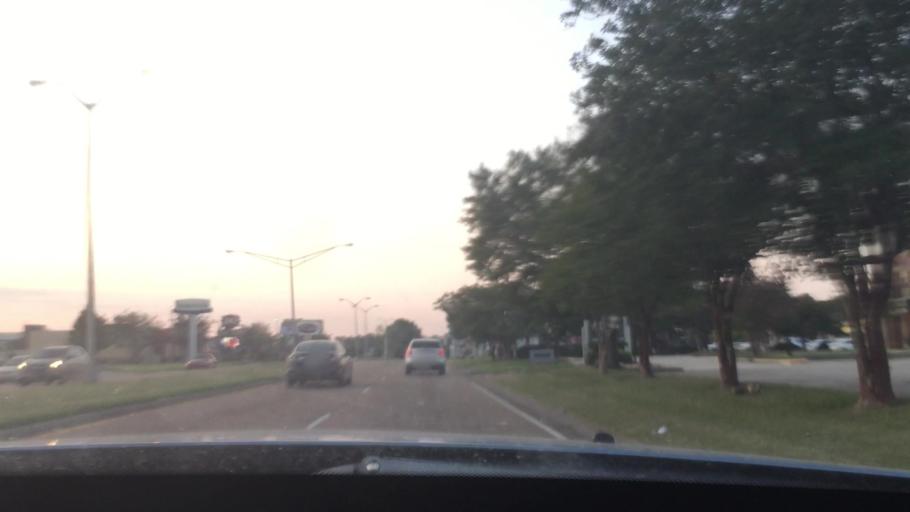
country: US
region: Louisiana
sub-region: East Baton Rouge Parish
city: Inniswold
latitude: 30.4207
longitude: -91.0515
